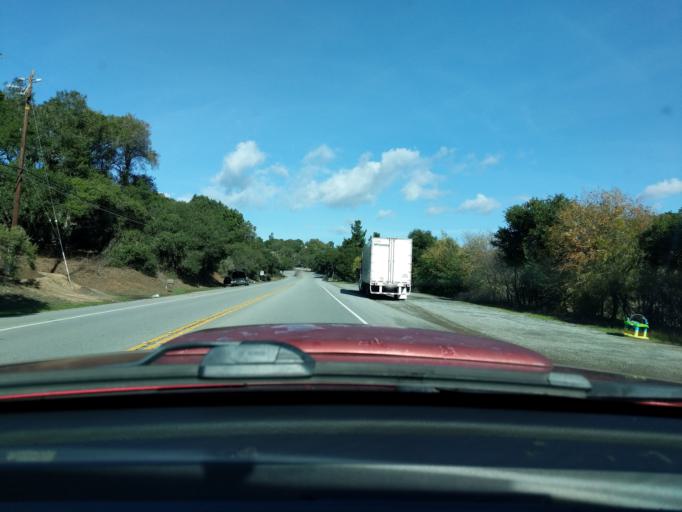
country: US
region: California
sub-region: San Benito County
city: Aromas
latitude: 36.8792
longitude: -121.6625
